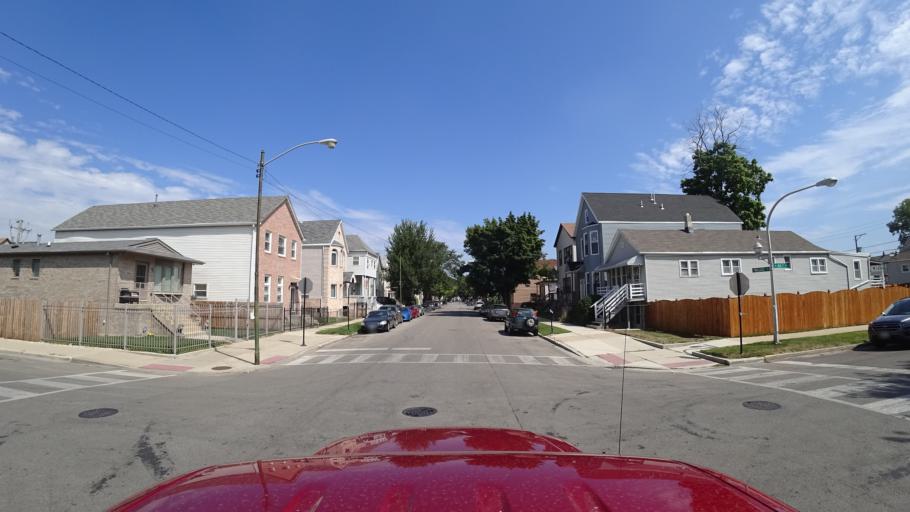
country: US
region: Illinois
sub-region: Cook County
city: Chicago
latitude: 41.8107
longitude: -87.6408
